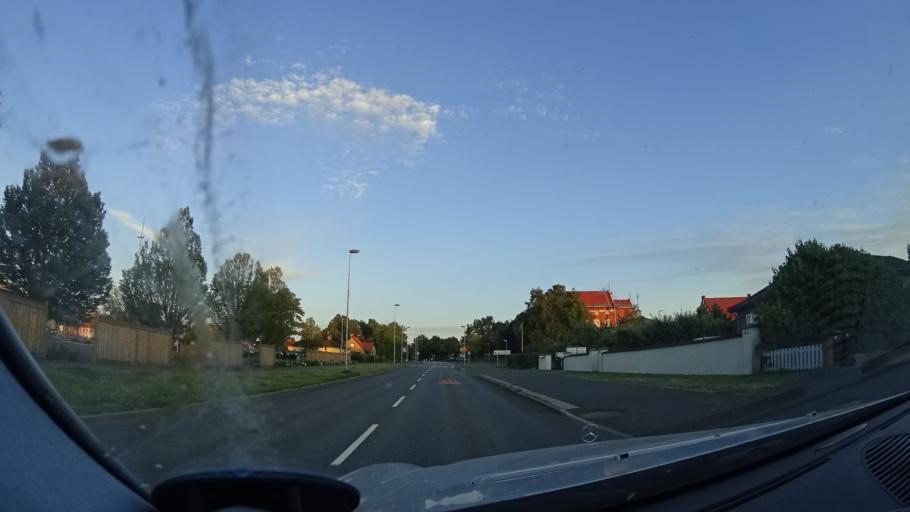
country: SE
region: Skane
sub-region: Kristianstads Kommun
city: Ahus
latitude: 55.9278
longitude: 14.2943
